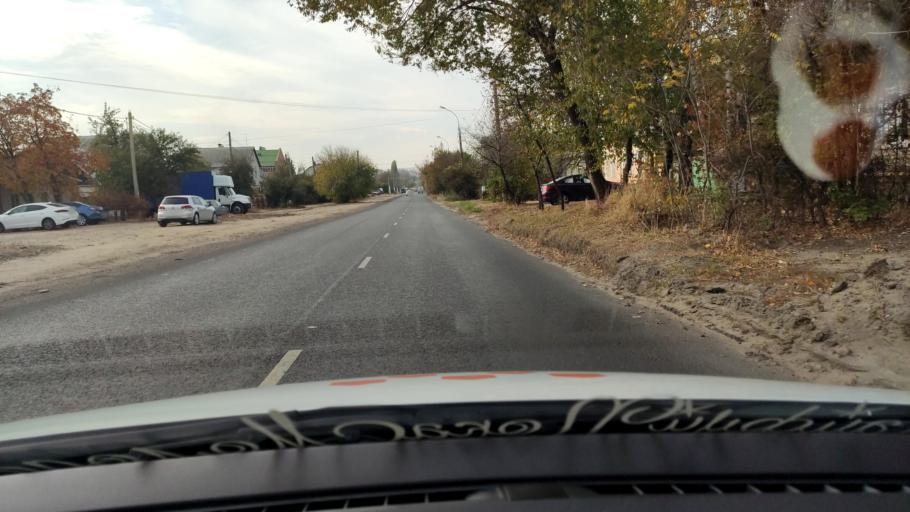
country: RU
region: Voronezj
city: Voronezh
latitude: 51.6980
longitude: 39.1783
